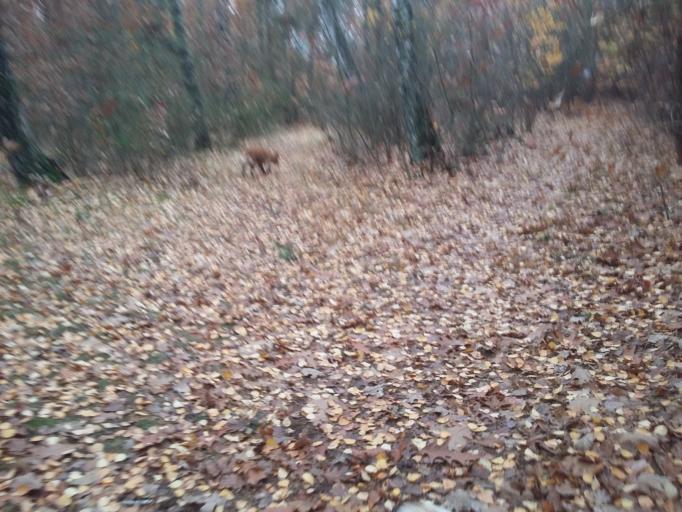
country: PL
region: Lodz Voivodeship
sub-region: Powiat pabianicki
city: Ksawerow
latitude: 51.7213
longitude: 19.3795
